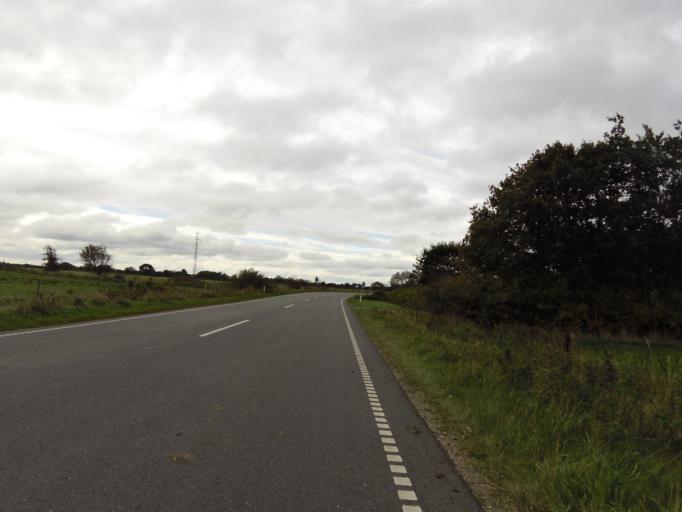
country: DK
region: South Denmark
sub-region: Tonder Kommune
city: Sherrebek
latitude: 55.2137
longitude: 8.8247
